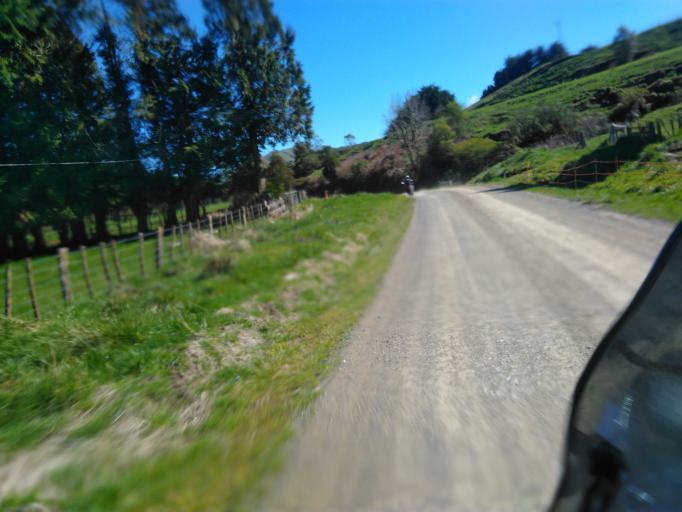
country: NZ
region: Bay of Plenty
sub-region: Opotiki District
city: Opotiki
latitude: -38.2915
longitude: 177.5471
